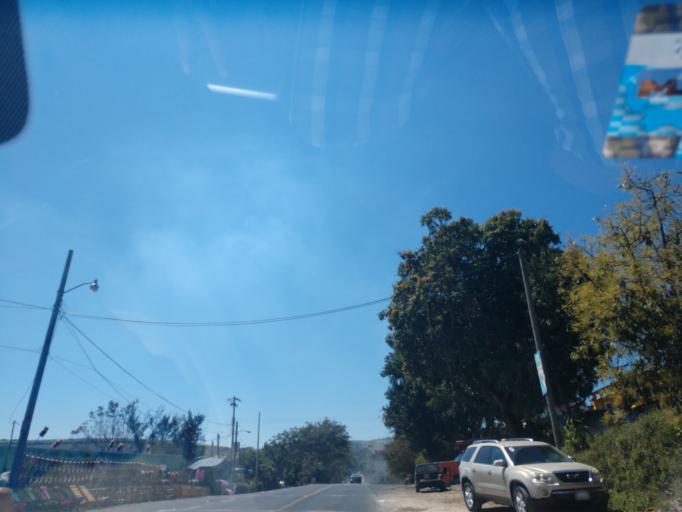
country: MX
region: Nayarit
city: Xalisco
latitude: 21.3831
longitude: -104.8895
